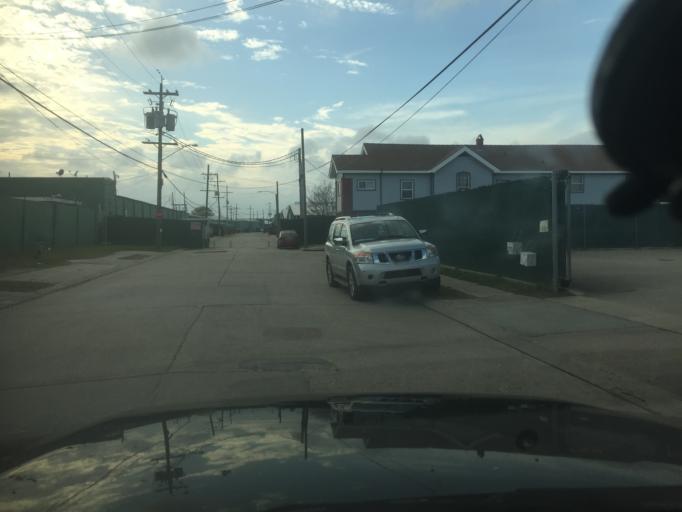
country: US
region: Louisiana
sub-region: Orleans Parish
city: New Orleans
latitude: 29.9860
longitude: -90.0818
